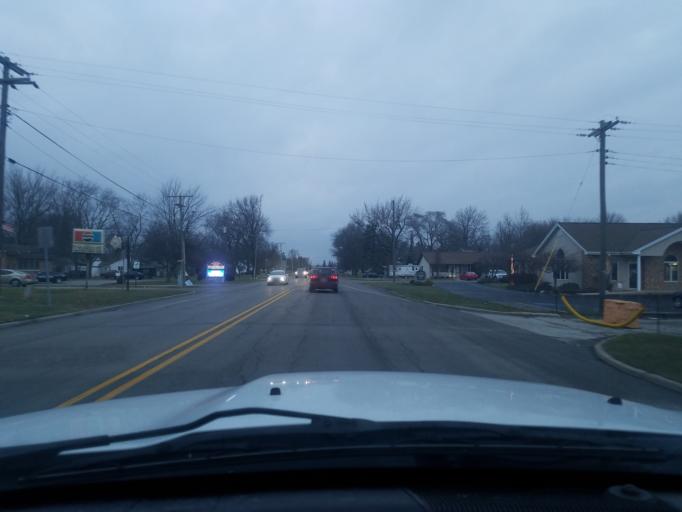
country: US
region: Indiana
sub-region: Wells County
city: Ossian
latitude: 40.8835
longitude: -85.1667
